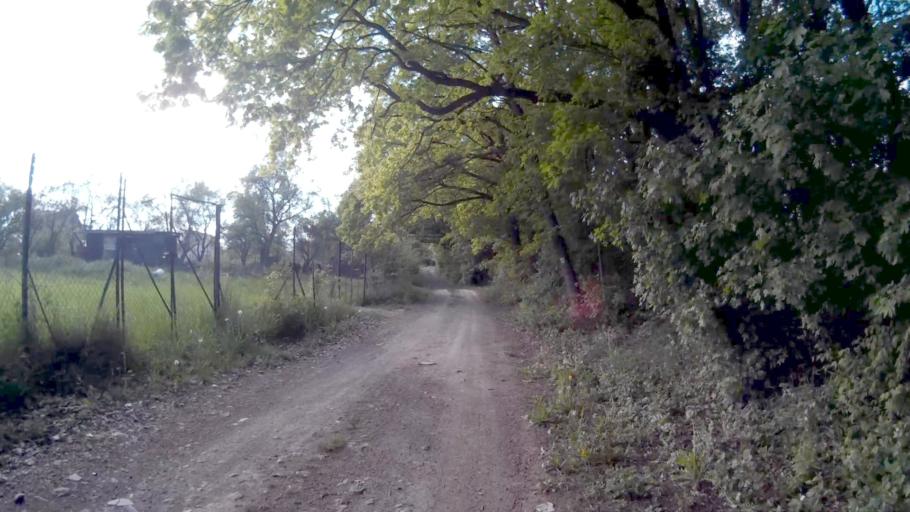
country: CZ
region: South Moravian
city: Troubsko
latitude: 49.1856
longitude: 16.5226
